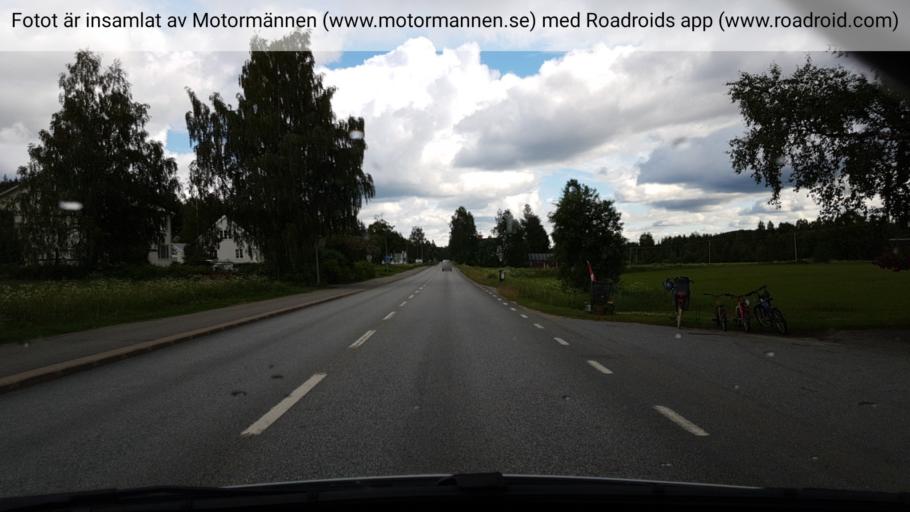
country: SE
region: Vaesterbotten
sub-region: Bjurholms Kommun
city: Bjurholm
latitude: 64.2459
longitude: 19.3204
